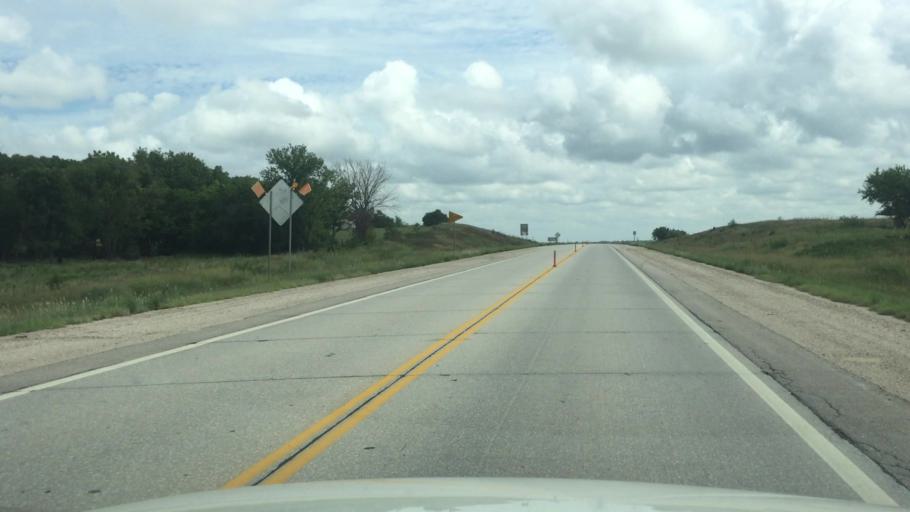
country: US
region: Kansas
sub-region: Allen County
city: Iola
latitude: 37.8863
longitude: -95.3915
